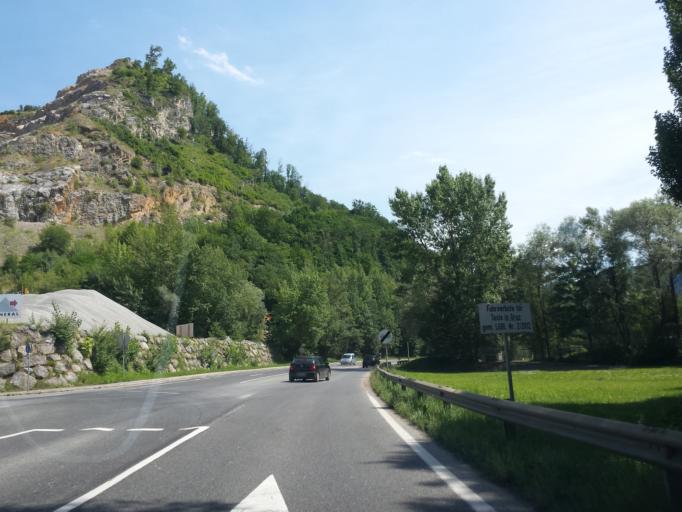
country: AT
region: Styria
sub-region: Politischer Bezirk Graz-Umgebung
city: Gratkorn
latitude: 47.1201
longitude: 15.3734
